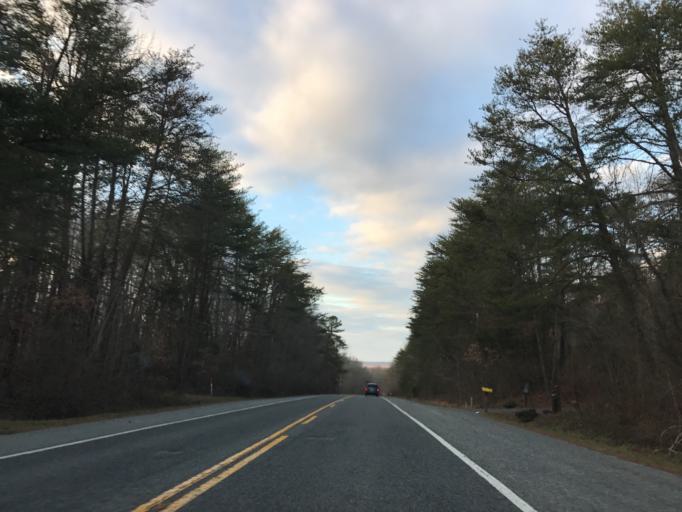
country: US
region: Maryland
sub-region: Cecil County
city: Charlestown
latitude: 39.5531
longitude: -75.9487
